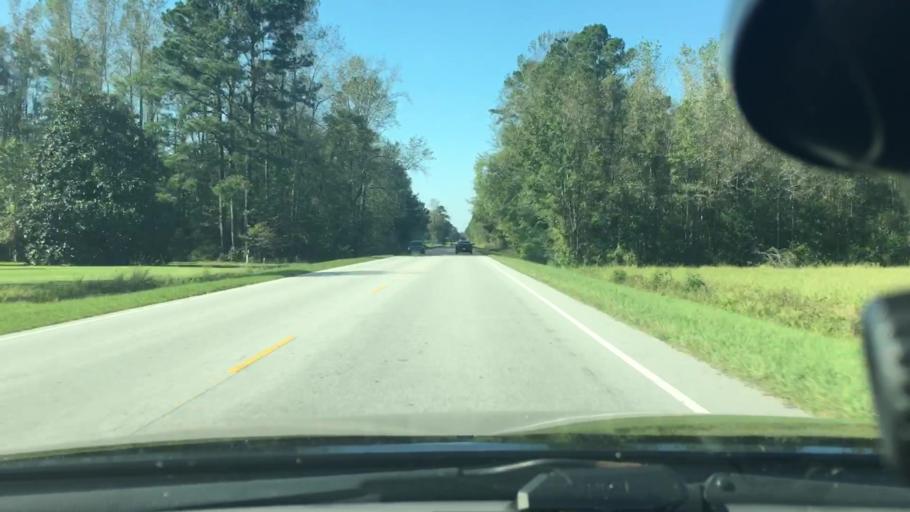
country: US
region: North Carolina
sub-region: Craven County
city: Vanceboro
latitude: 35.3027
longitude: -77.1334
